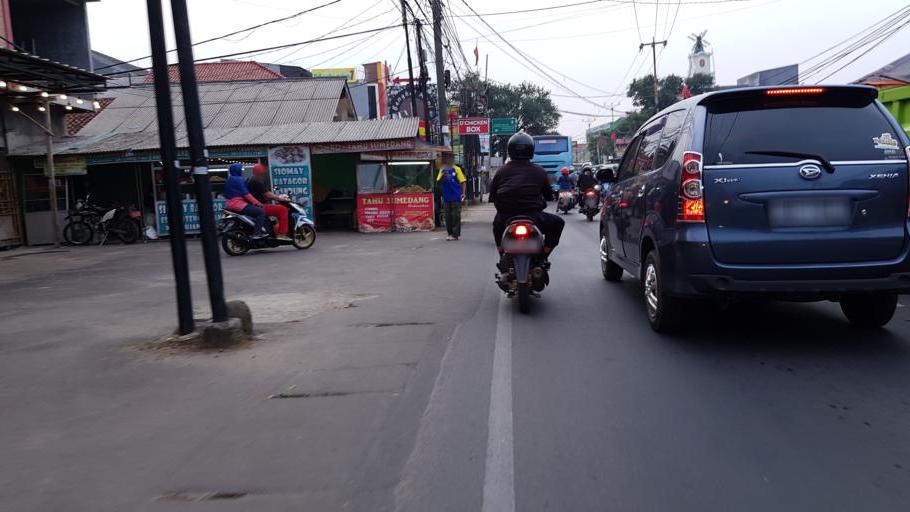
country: ID
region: West Java
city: Sawangan
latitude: -6.3954
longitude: 106.7742
